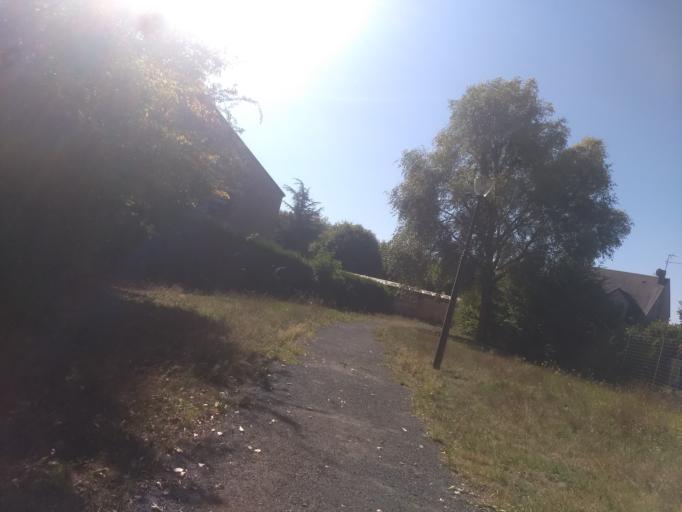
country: FR
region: Nord-Pas-de-Calais
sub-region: Departement du Pas-de-Calais
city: Achicourt
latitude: 50.2851
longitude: 2.7475
